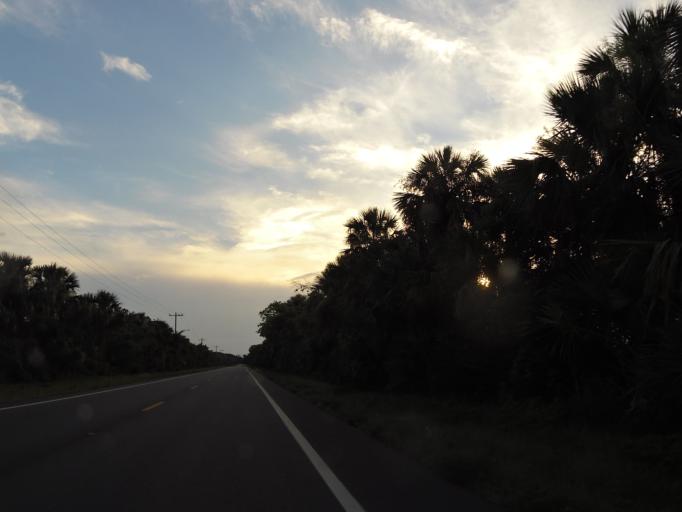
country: US
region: Florida
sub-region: Duval County
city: Atlantic Beach
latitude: 30.3993
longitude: -81.4891
